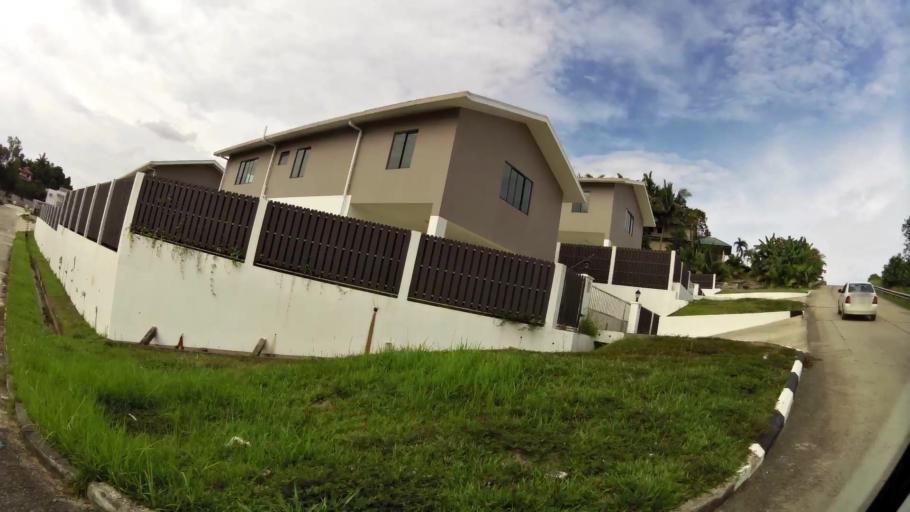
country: BN
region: Brunei and Muara
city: Bandar Seri Begawan
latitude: 4.8950
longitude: 114.8946
